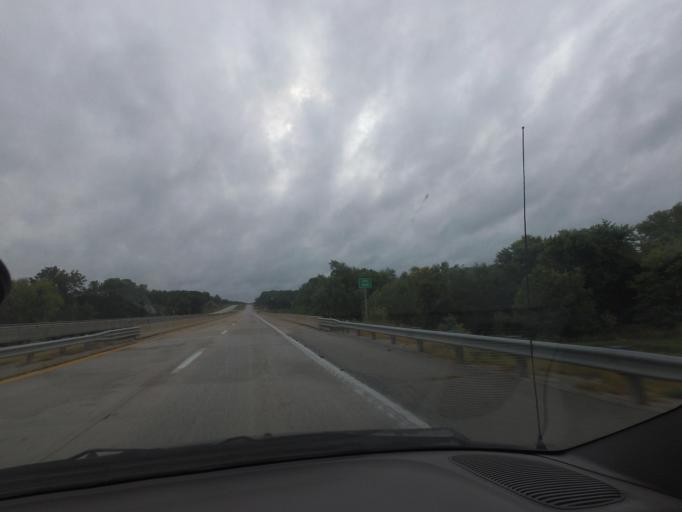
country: US
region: Missouri
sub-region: Shelby County
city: Shelbina
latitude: 39.6680
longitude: -91.9041
